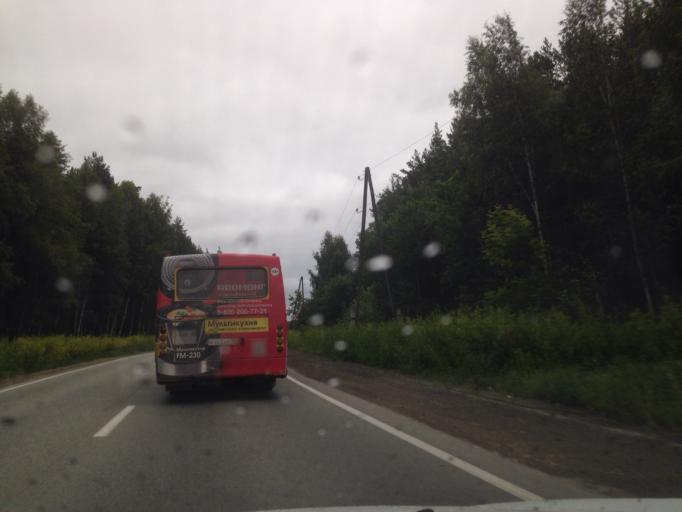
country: RU
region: Sverdlovsk
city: Istok
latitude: 56.8454
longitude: 60.7207
